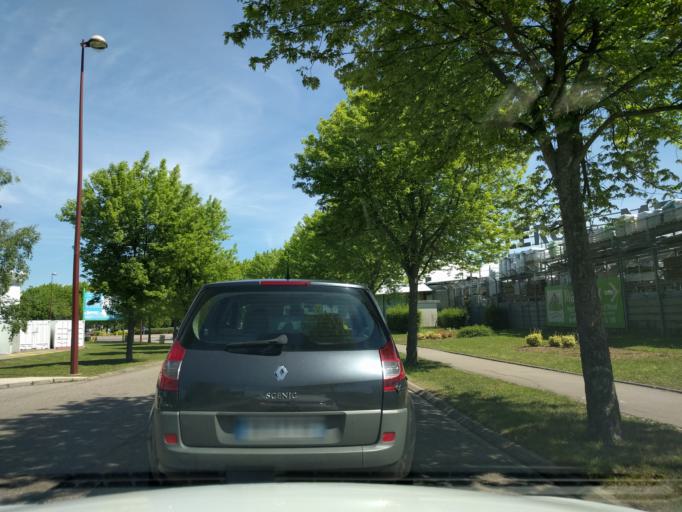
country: FR
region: Lorraine
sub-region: Departement de la Moselle
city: Peltre
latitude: 49.1051
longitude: 6.2313
